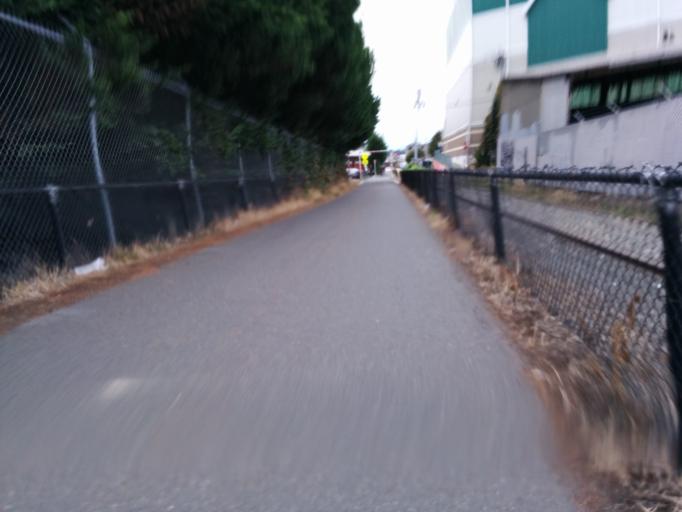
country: US
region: Washington
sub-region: King County
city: Seattle
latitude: 47.6574
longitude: -122.3644
